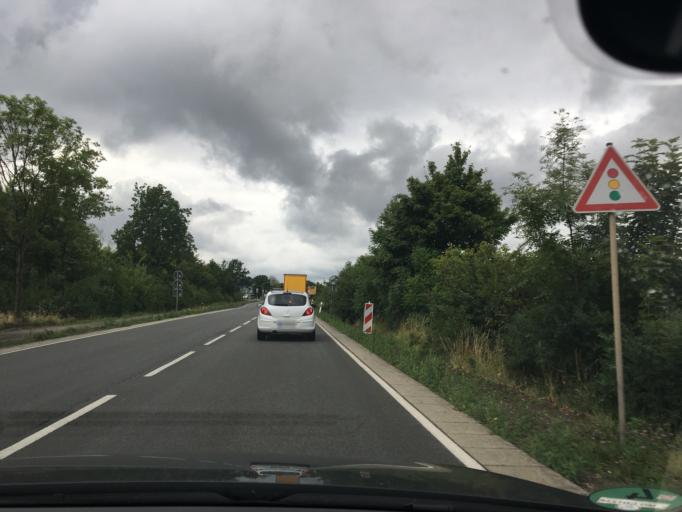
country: DE
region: North Rhine-Westphalia
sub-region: Regierungsbezirk Koln
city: Kreuzau
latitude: 50.7654
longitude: 6.5242
